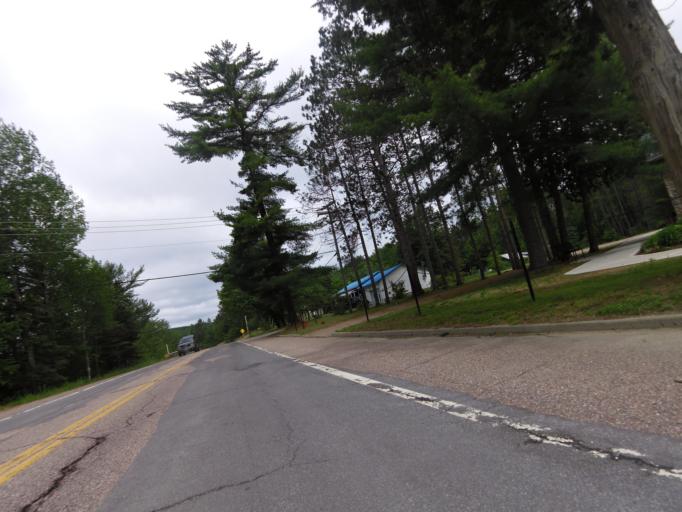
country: CA
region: Quebec
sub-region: Outaouais
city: Shawville
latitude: 45.8387
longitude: -76.4501
